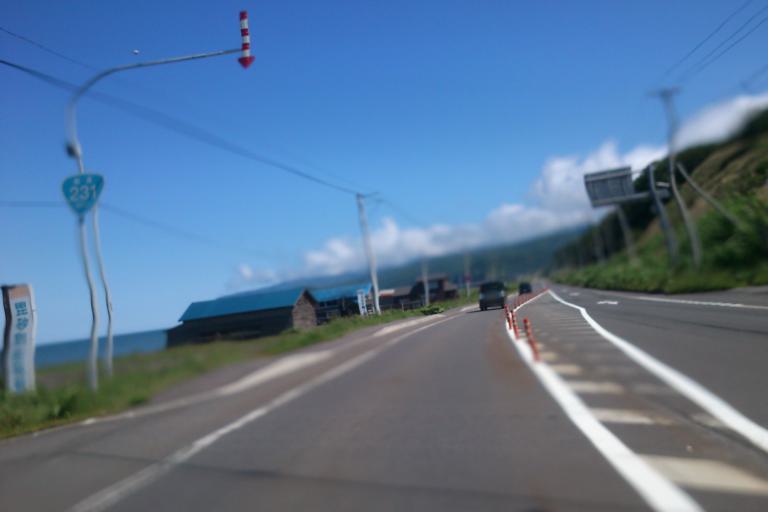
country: JP
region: Hokkaido
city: Ishikari
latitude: 43.5607
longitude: 141.3787
